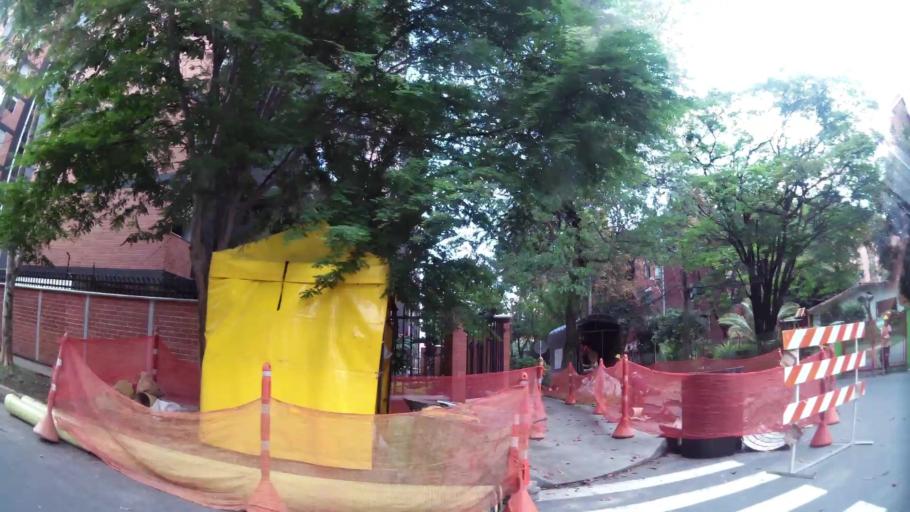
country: CO
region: Antioquia
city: Envigado
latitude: 6.1803
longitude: -75.5860
